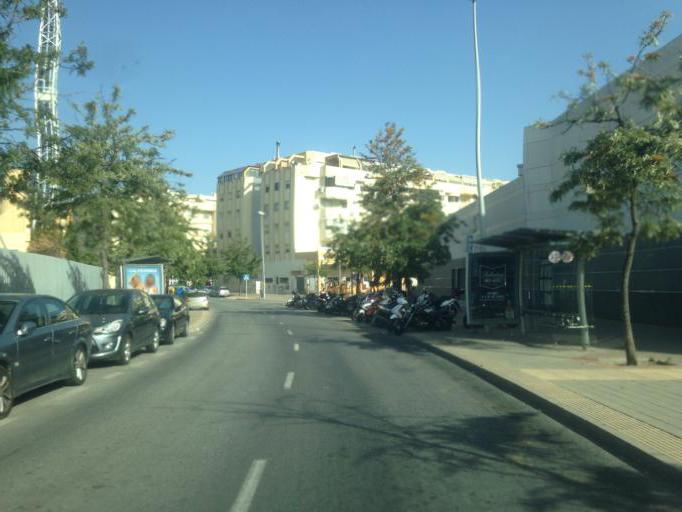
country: ES
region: Andalusia
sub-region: Provincia de Malaga
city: Malaga
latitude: 36.7084
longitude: -4.4618
